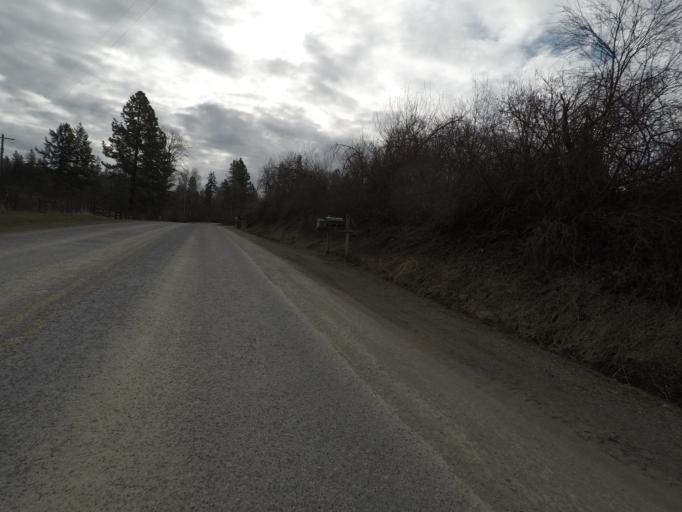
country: US
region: Washington
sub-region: Stevens County
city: Colville
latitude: 48.5109
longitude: -117.8671
